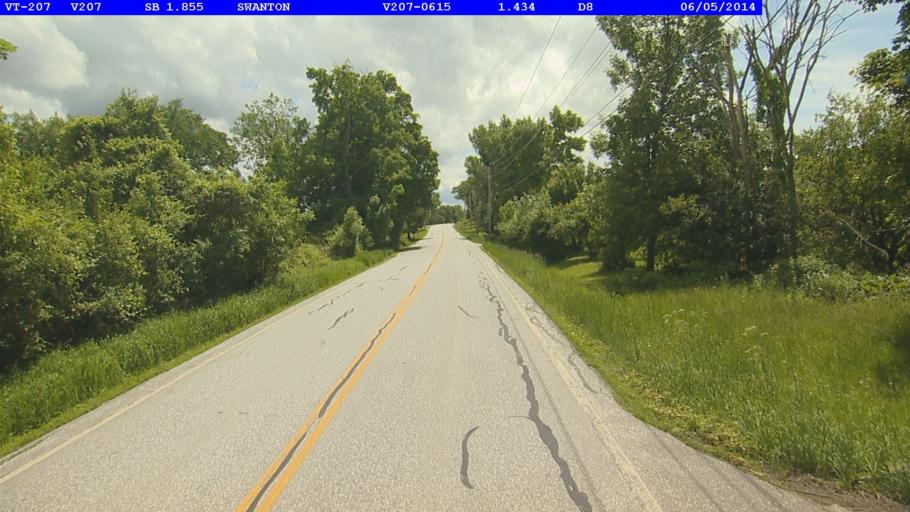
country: US
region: Vermont
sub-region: Franklin County
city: Saint Albans
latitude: 44.8658
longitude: -73.0753
